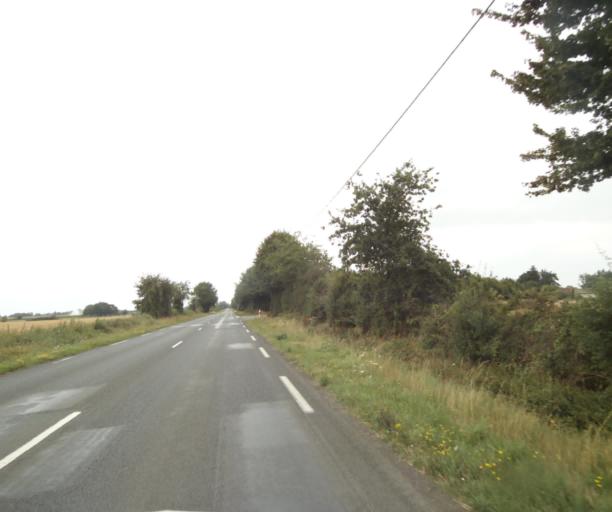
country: FR
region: Pays de la Loire
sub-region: Departement de la Sarthe
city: Vion
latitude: 47.8387
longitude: -0.2470
